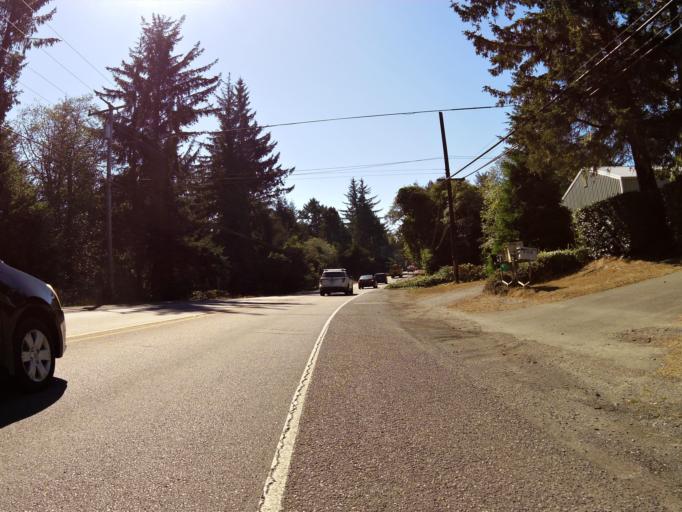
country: US
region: Oregon
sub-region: Coos County
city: Barview
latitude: 43.3500
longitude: -124.3137
